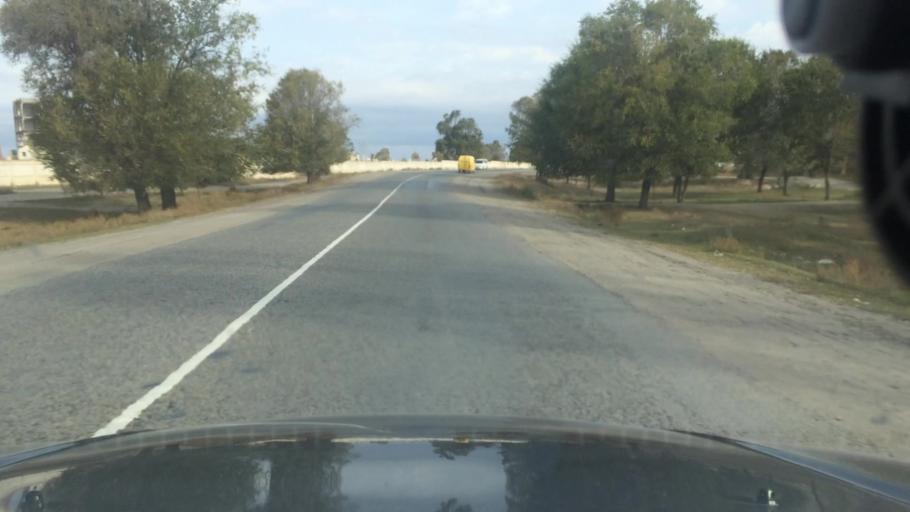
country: KG
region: Ysyk-Koel
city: Karakol
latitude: 42.5358
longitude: 78.3819
